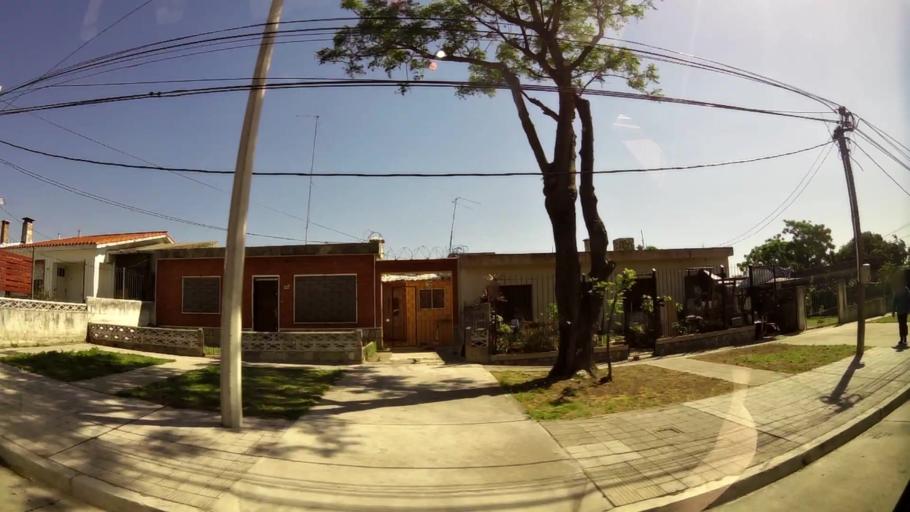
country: UY
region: Montevideo
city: Montevideo
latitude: -34.8431
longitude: -56.2412
